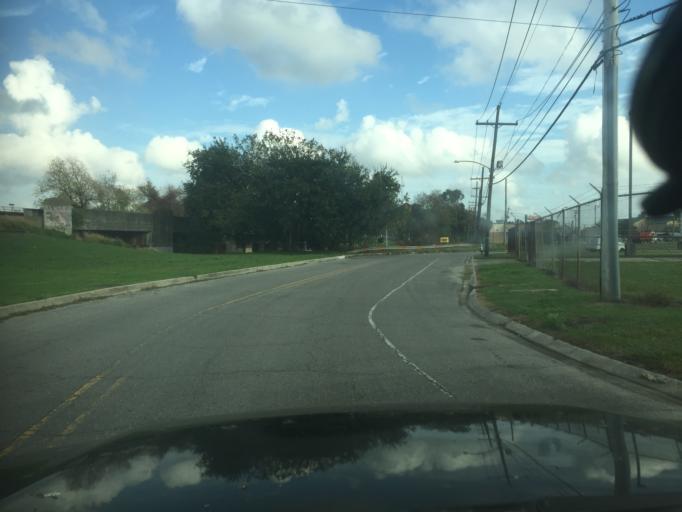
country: US
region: Louisiana
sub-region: Orleans Parish
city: New Orleans
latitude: 29.9920
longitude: -90.0776
